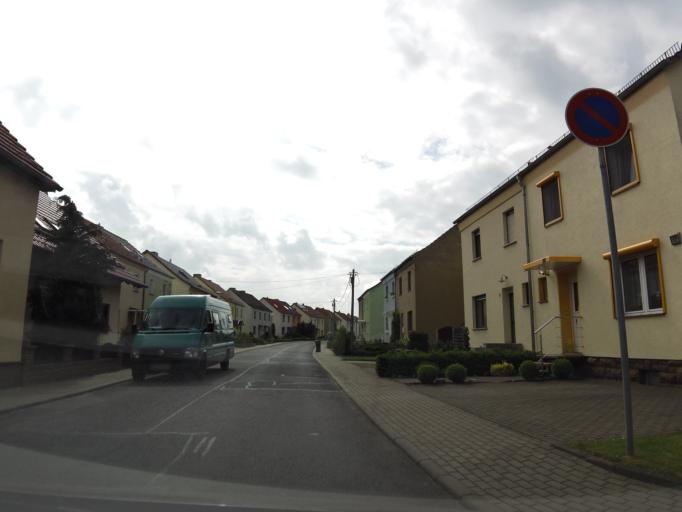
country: DE
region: Thuringia
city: Horselgau
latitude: 50.9193
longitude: 10.5881
